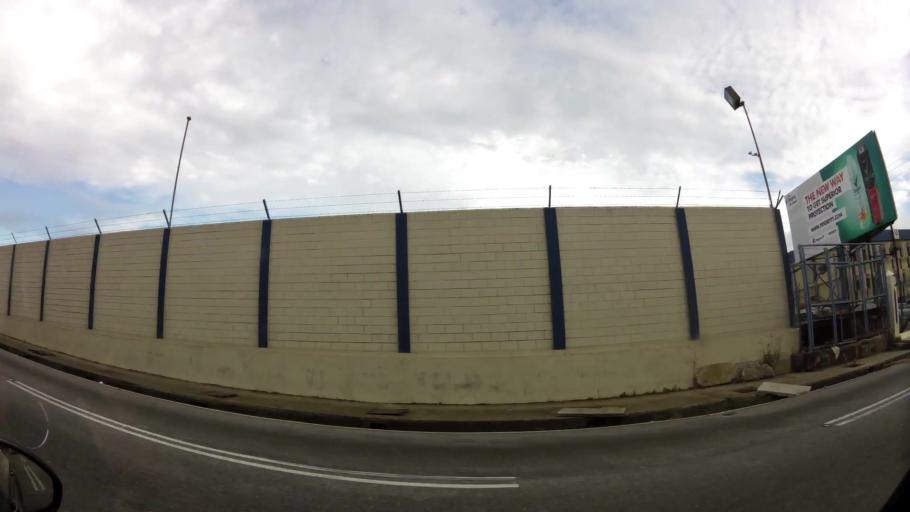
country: TT
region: Tunapuna/Piarco
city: Tunapuna
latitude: 10.6501
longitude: -61.4280
